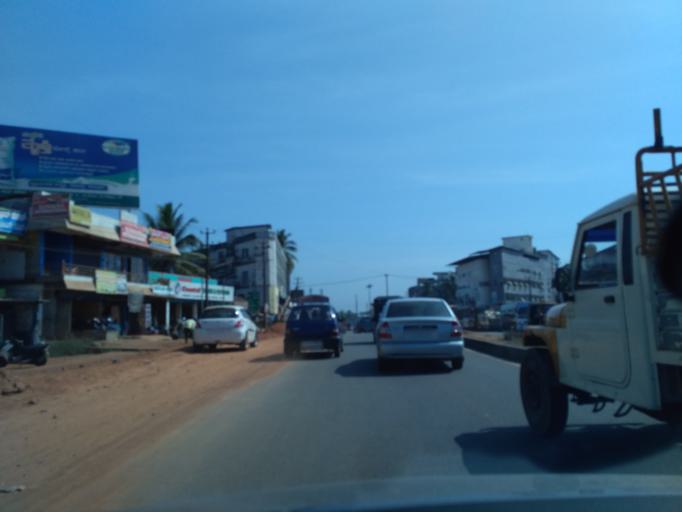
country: IN
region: Karnataka
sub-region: Dakshina Kannada
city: Bantval
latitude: 12.8801
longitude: 75.0210
